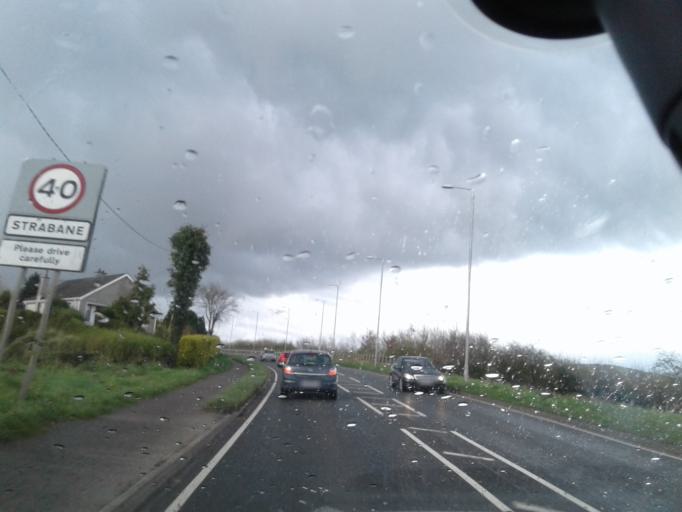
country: GB
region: Northern Ireland
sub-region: Strabane District
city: Sion Mills
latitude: 54.8004
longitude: -7.4740
